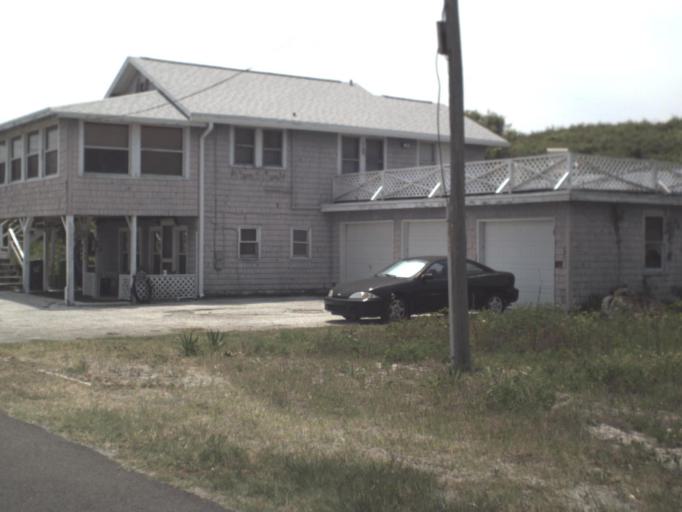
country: US
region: Florida
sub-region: Nassau County
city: Fernandina Beach
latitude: 30.6303
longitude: -81.4389
